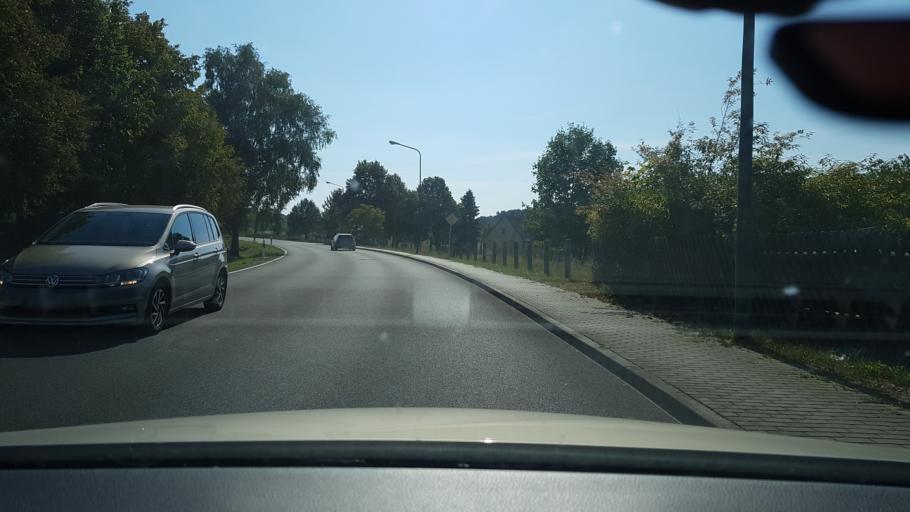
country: DE
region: Brandenburg
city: Mixdorf
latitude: 52.1423
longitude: 14.4166
